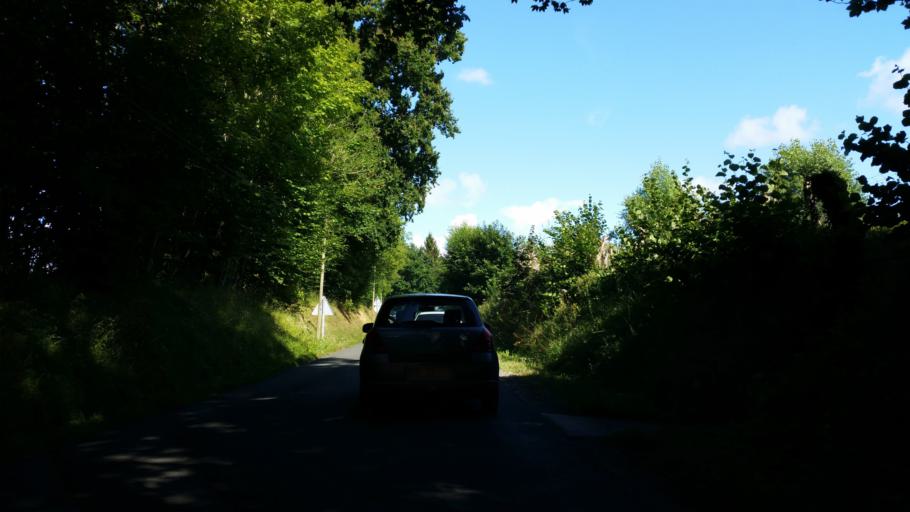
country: FR
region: Lower Normandy
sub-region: Departement du Calvados
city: Saint-Gatien-des-Bois
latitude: 49.3643
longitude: 0.1993
